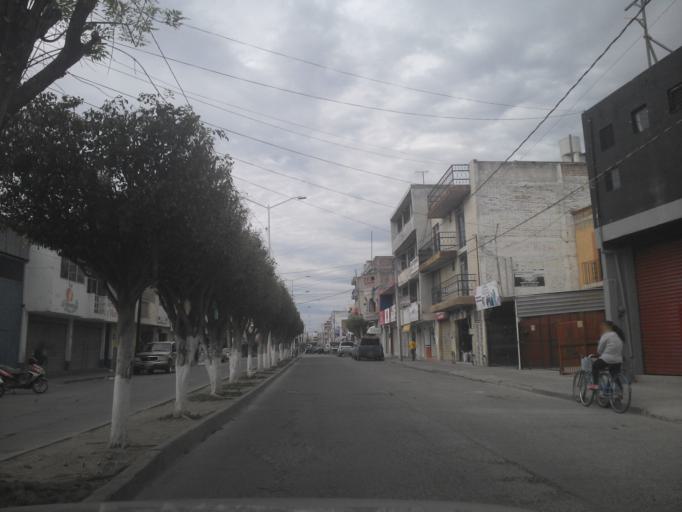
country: MX
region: Guanajuato
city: San Francisco del Rincon
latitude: 21.0130
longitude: -101.8574
